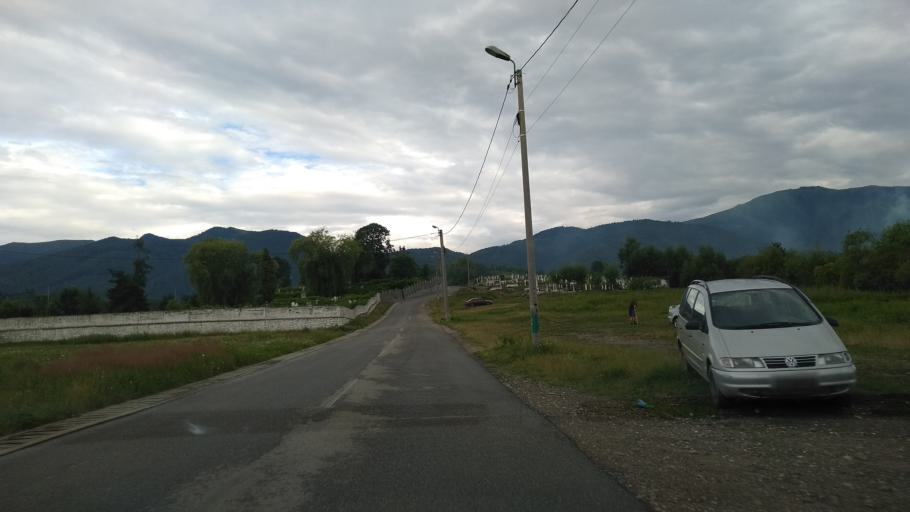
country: RO
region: Hunedoara
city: Vulcan
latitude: 45.3697
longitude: 23.2822
